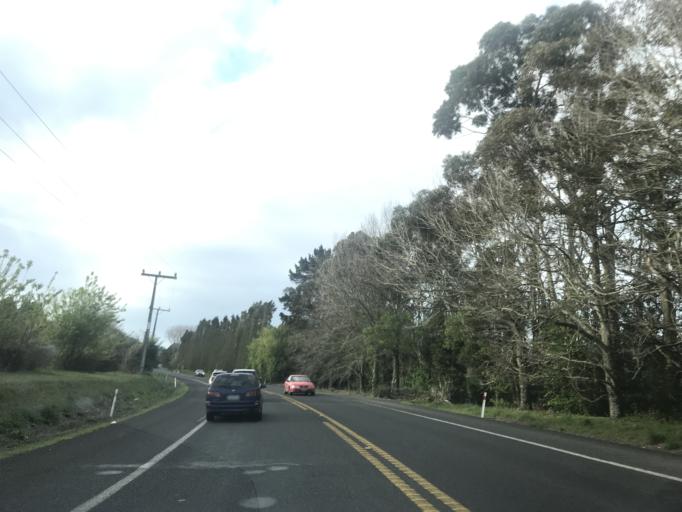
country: NZ
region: Bay of Plenty
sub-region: Western Bay of Plenty District
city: Katikati
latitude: -37.5225
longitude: 175.9201
